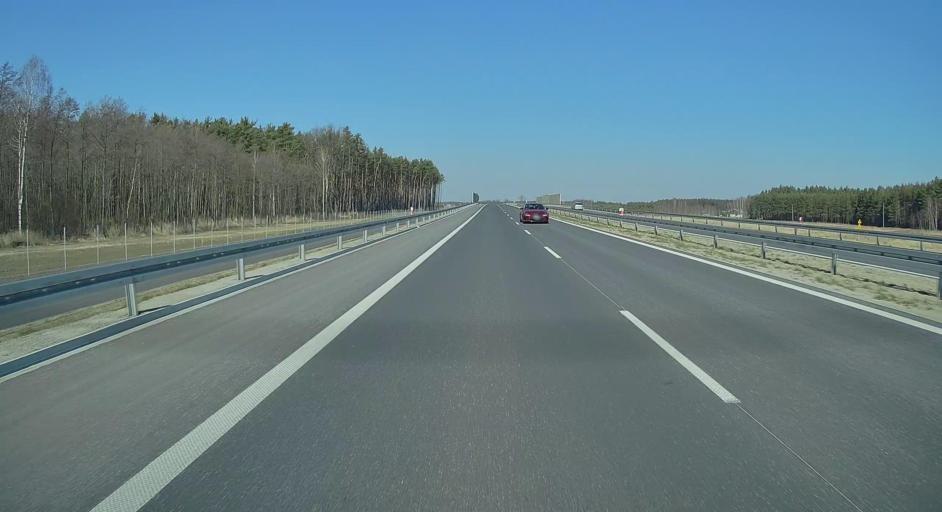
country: PL
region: Subcarpathian Voivodeship
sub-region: Powiat lezajski
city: Letownia
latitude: 50.3551
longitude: 22.1976
